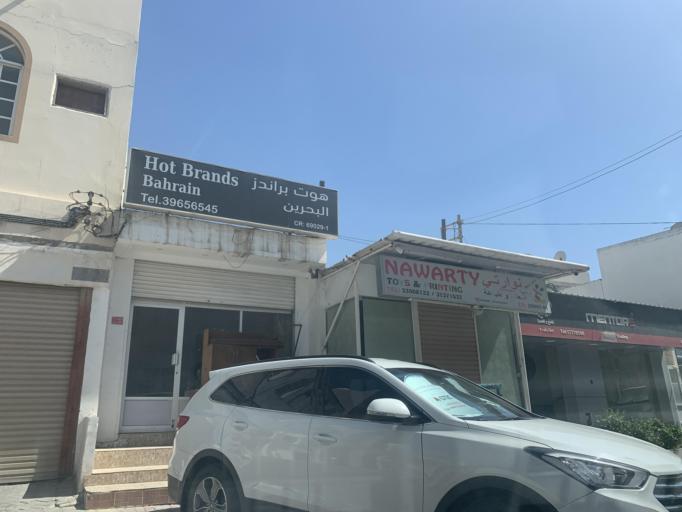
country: BH
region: Manama
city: Jidd Hafs
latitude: 26.2131
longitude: 50.5639
